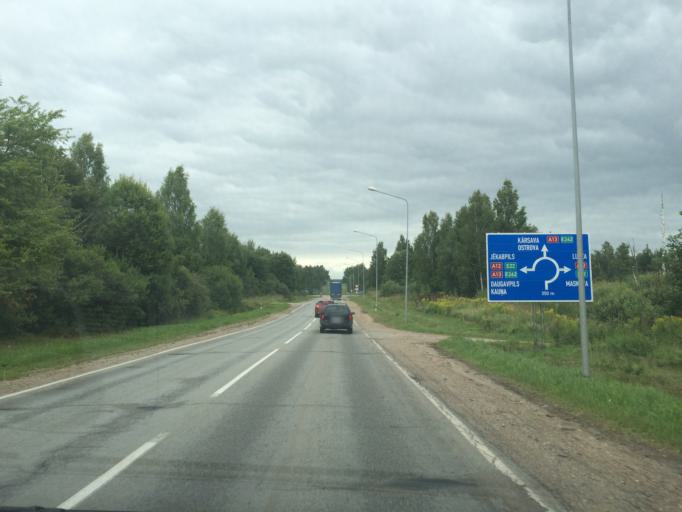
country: LV
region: Rezekne
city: Rezekne
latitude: 56.5413
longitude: 27.3522
